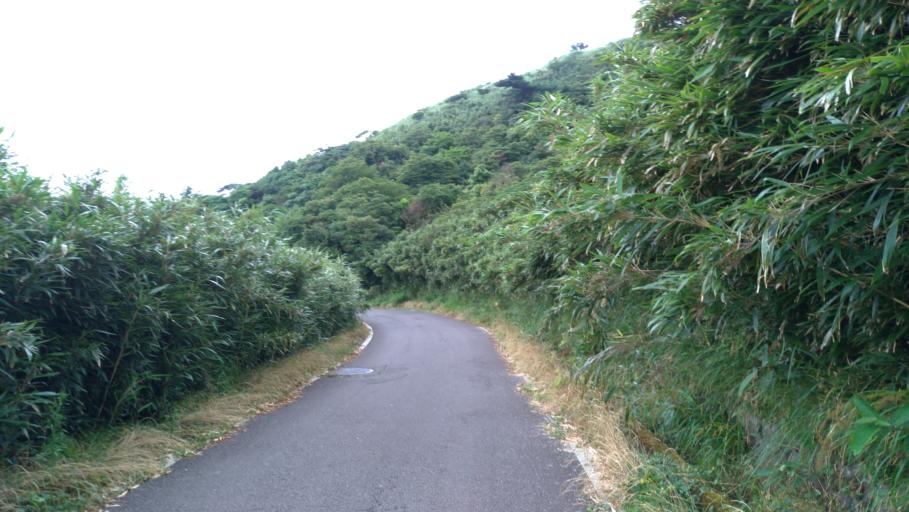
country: TW
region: Taipei
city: Taipei
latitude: 25.1779
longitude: 121.5214
